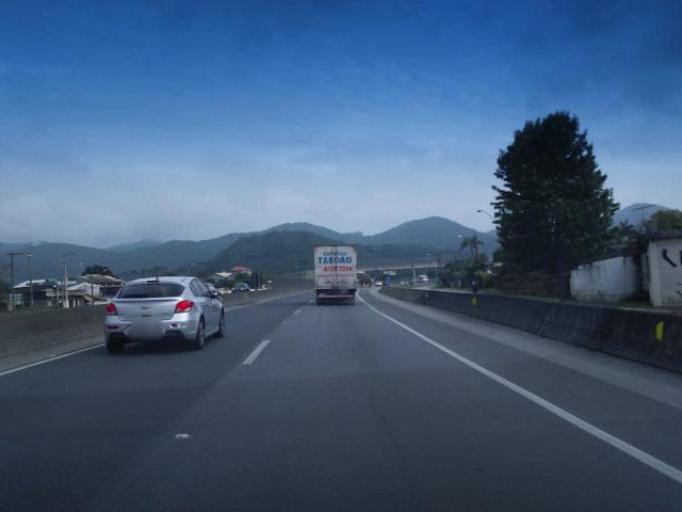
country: BR
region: Santa Catarina
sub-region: Itapema
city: Itapema
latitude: -27.1017
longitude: -48.6178
